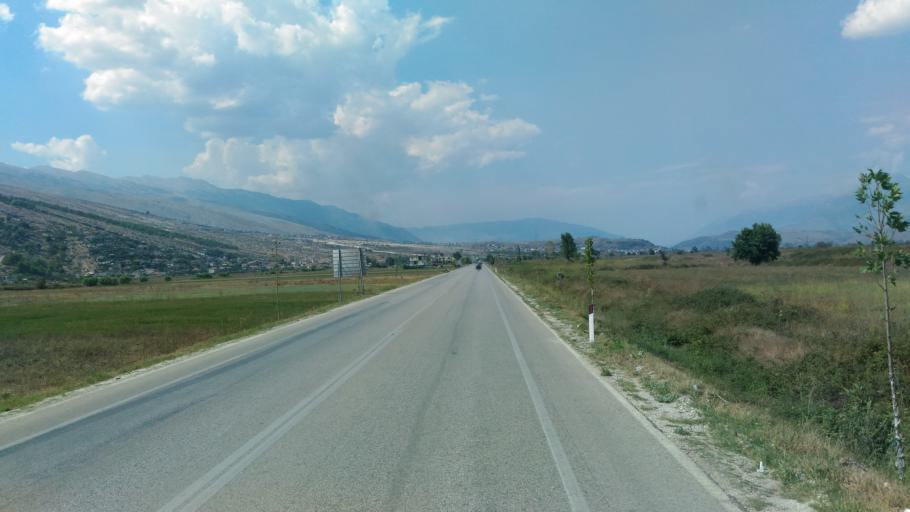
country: AL
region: Gjirokaster
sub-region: Rrethi i Gjirokastres
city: Dervician
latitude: 40.0228
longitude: 20.1922
